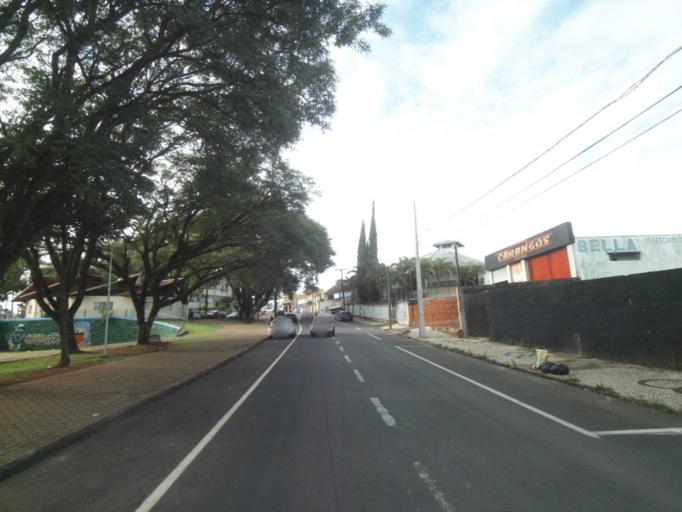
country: BR
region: Parana
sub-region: Telemaco Borba
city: Telemaco Borba
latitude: -24.3323
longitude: -50.6264
